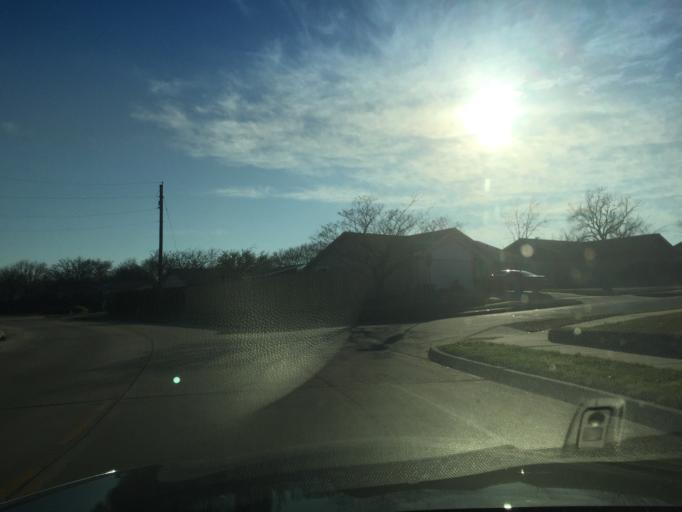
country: US
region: Texas
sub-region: Dallas County
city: Carrollton
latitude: 32.9911
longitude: -96.8844
